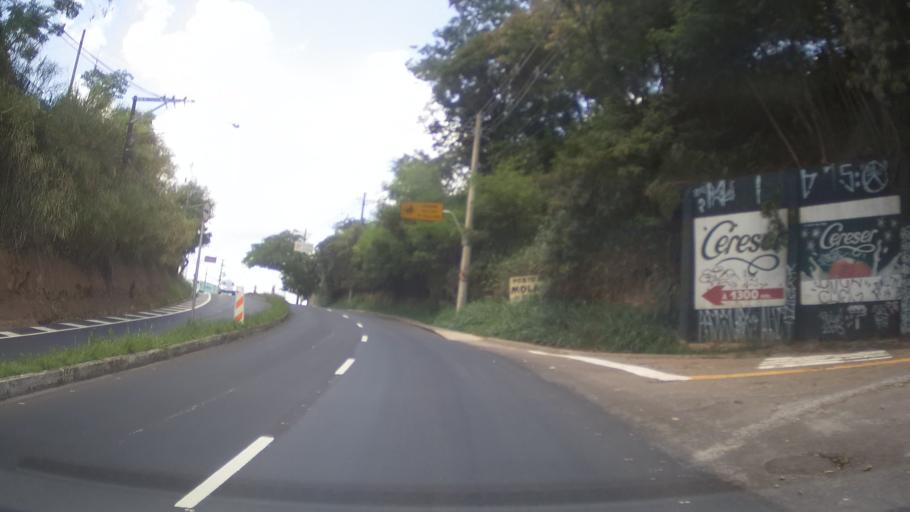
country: BR
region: Sao Paulo
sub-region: Jundiai
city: Jundiai
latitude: -23.1537
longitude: -46.8586
